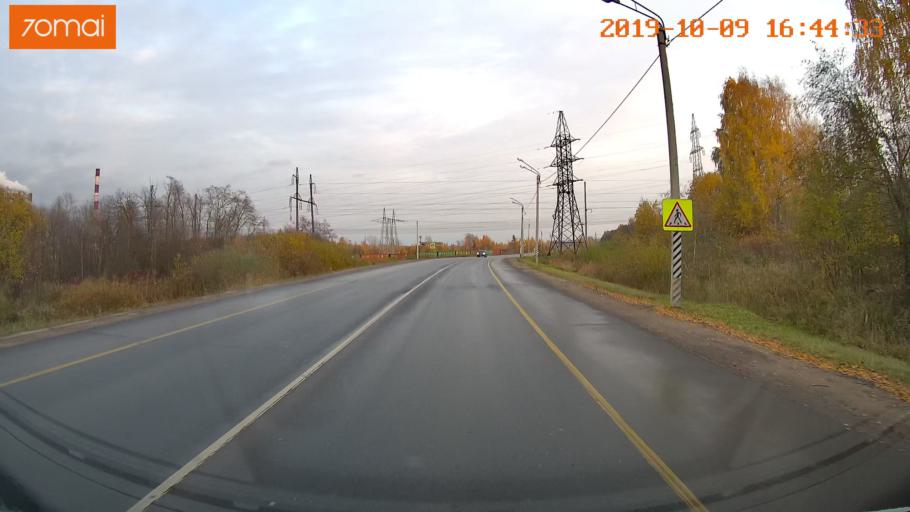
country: RU
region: Kostroma
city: Volgorechensk
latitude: 57.4513
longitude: 41.1425
